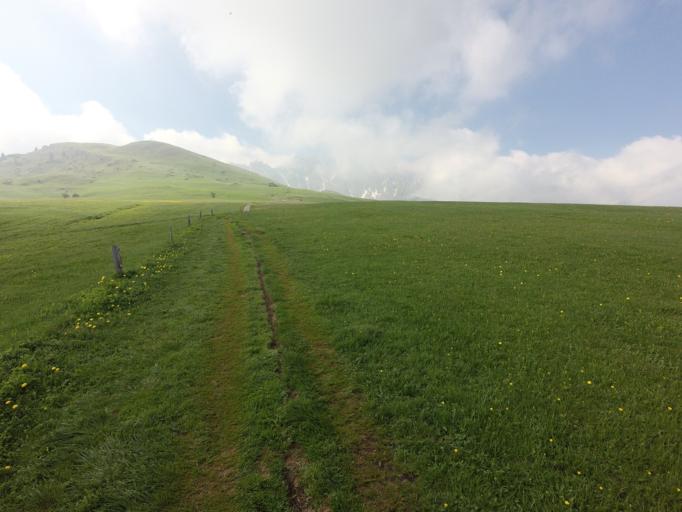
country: IT
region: Trentino-Alto Adige
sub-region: Bolzano
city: Ortisei
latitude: 46.5229
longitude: 11.6317
